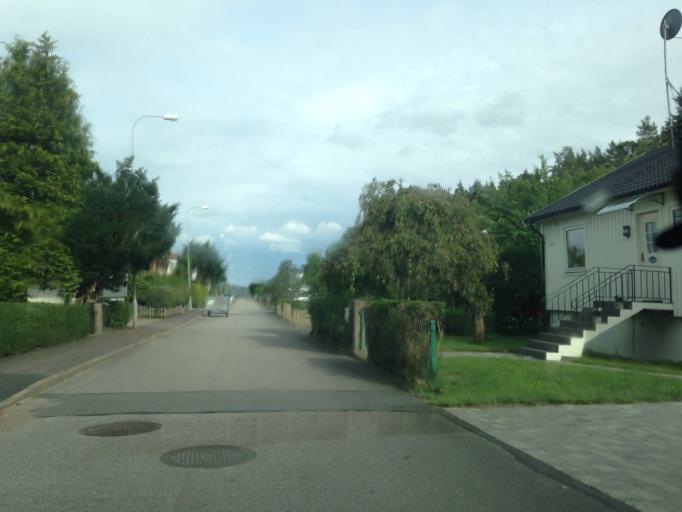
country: SE
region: Vaestra Goetaland
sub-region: Goteborg
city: Goeteborg
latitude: 57.7513
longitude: 11.9688
